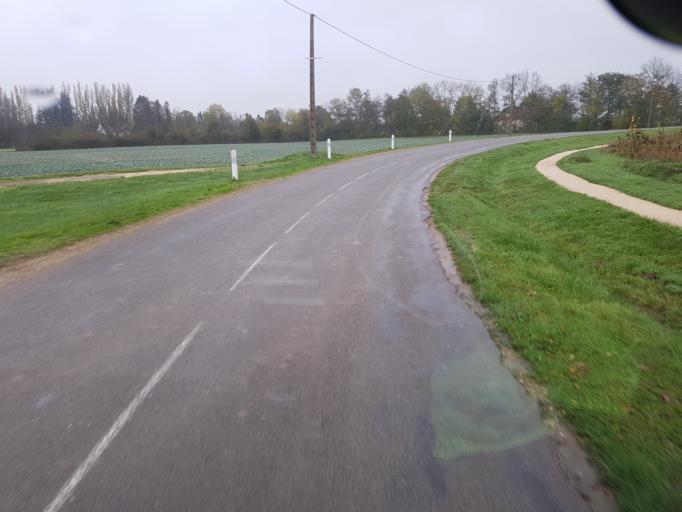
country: FR
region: Bourgogne
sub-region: Departement de la Cote-d'Or
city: Genlis
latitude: 47.2736
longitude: 5.2168
